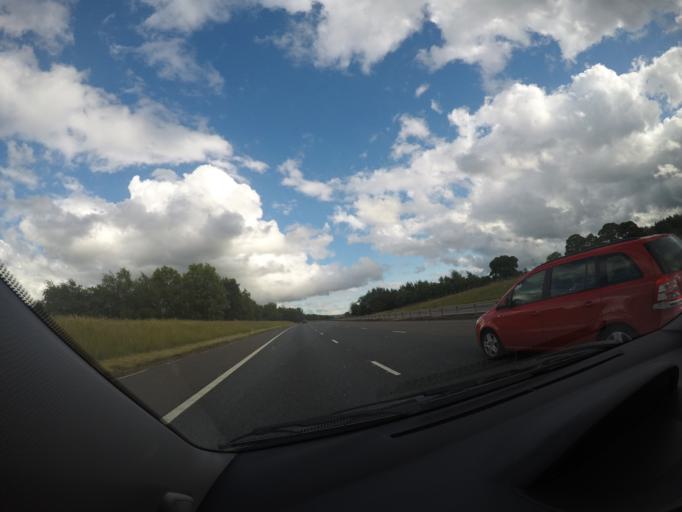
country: GB
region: Scotland
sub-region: Dumfries and Galloway
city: Lochmaben
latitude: 55.1746
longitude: -3.3989
